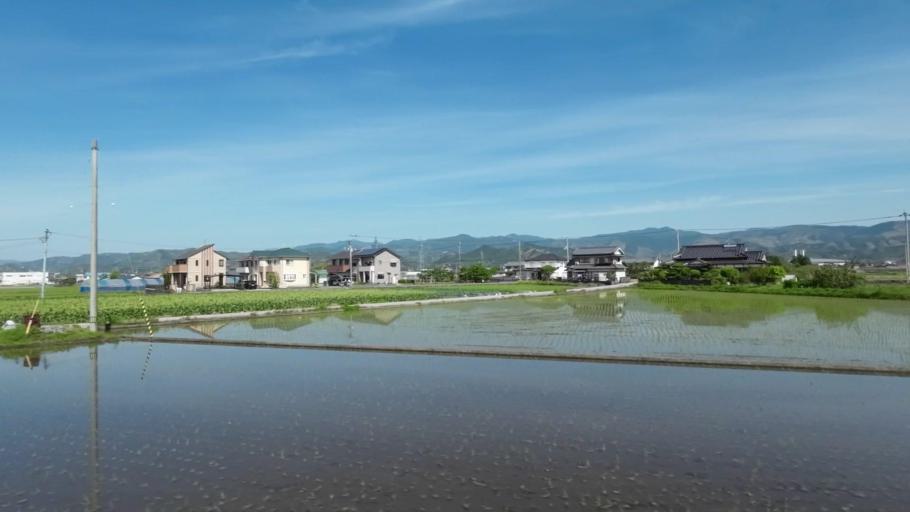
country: JP
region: Kochi
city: Kochi-shi
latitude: 33.5865
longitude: 133.6562
